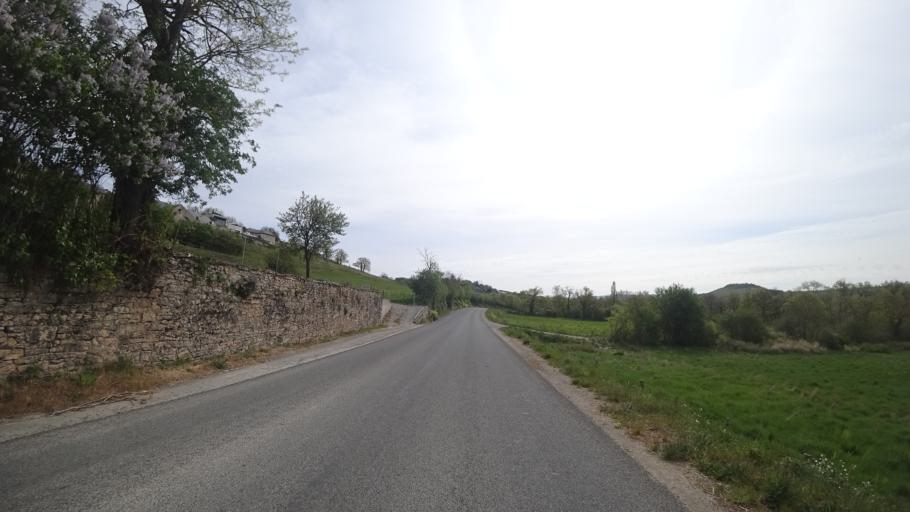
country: FR
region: Midi-Pyrenees
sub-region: Departement de l'Aveyron
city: Sebazac-Concoures
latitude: 44.3812
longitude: 2.5991
